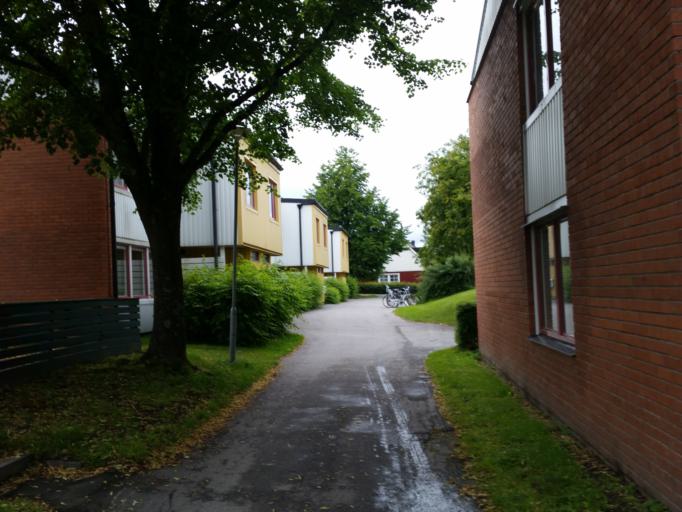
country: SE
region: Vaesterbotten
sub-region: Umea Kommun
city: Ersmark
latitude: 63.8459
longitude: 20.3021
